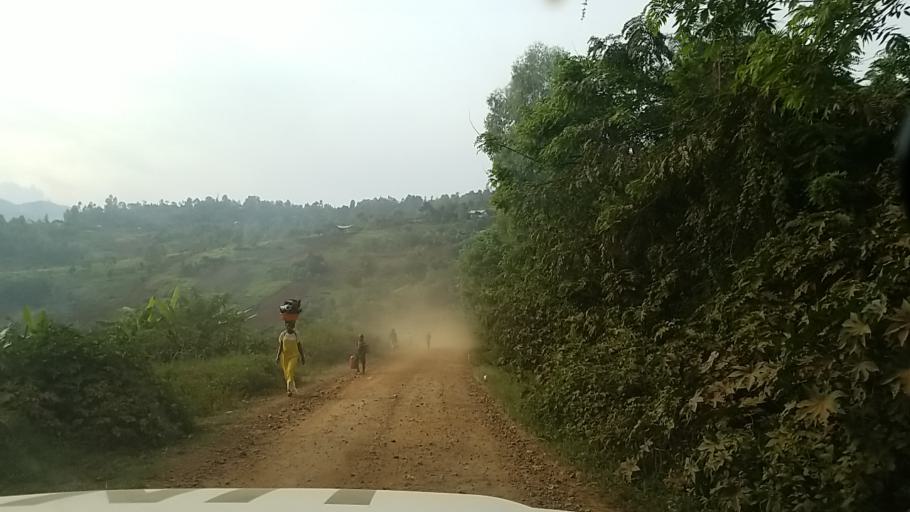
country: RW
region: Western Province
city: Cyangugu
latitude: -2.1051
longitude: 28.9170
